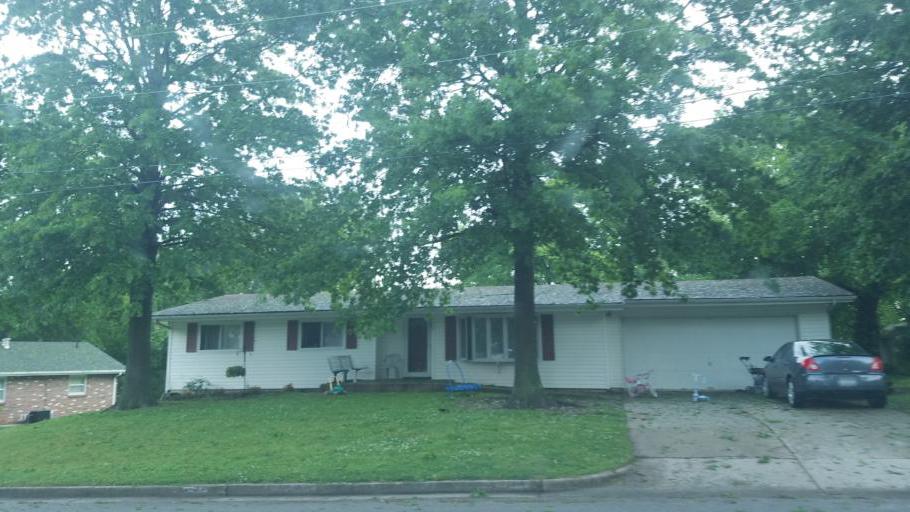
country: US
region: Missouri
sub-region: Moniteau County
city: California
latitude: 38.6252
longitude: -92.5736
